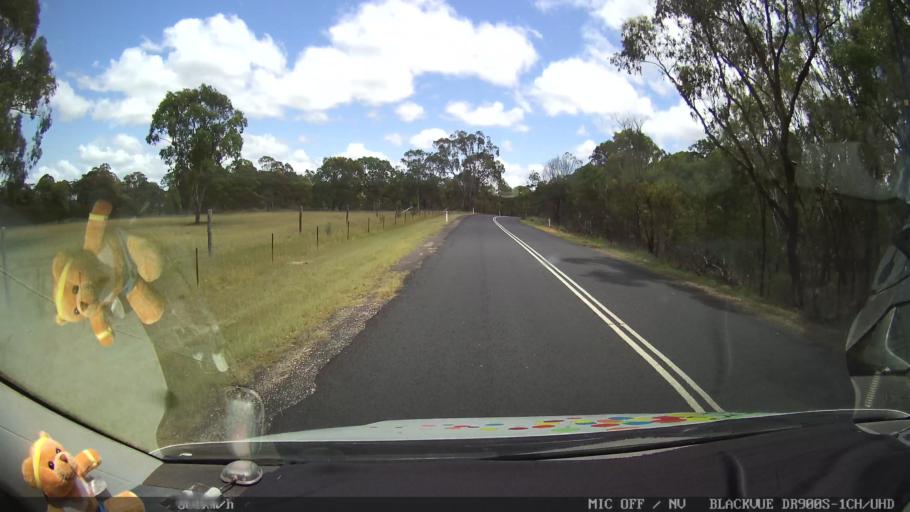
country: AU
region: New South Wales
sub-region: Glen Innes Severn
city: Glen Innes
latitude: -29.4671
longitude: 151.6213
